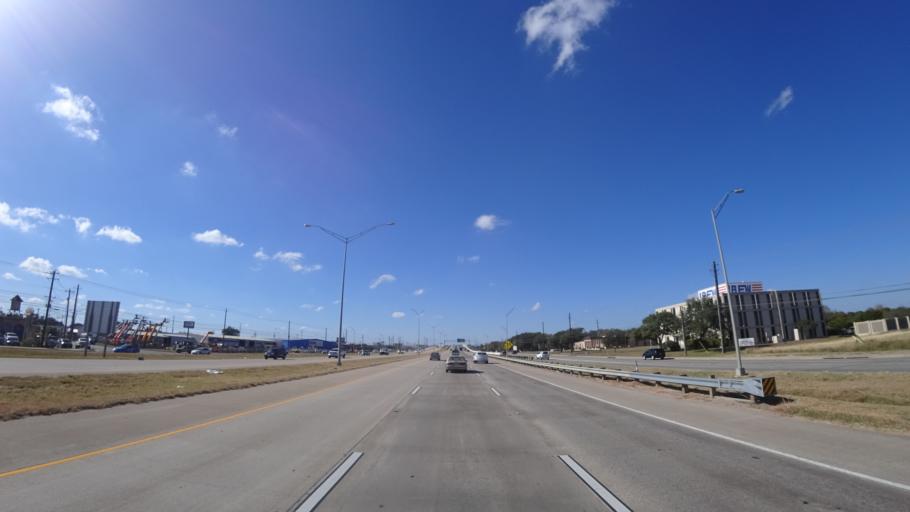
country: US
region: Texas
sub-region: Travis County
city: Austin
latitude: 30.2143
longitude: -97.7276
